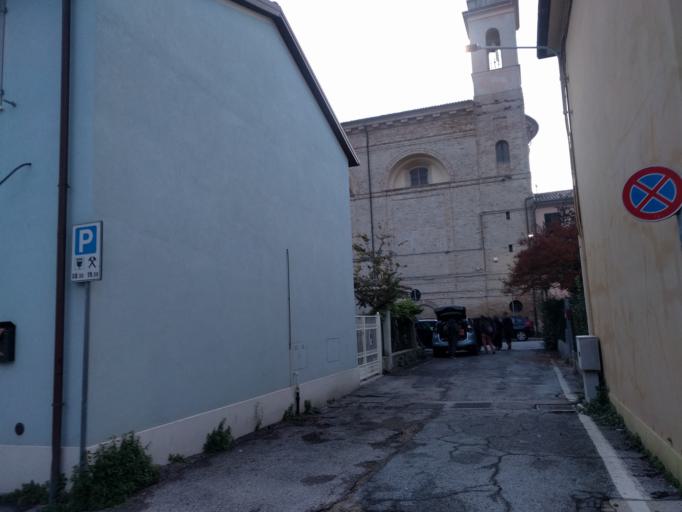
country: IT
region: The Marches
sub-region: Provincia di Ancona
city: Senigallia
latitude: 43.7171
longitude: 13.2167
